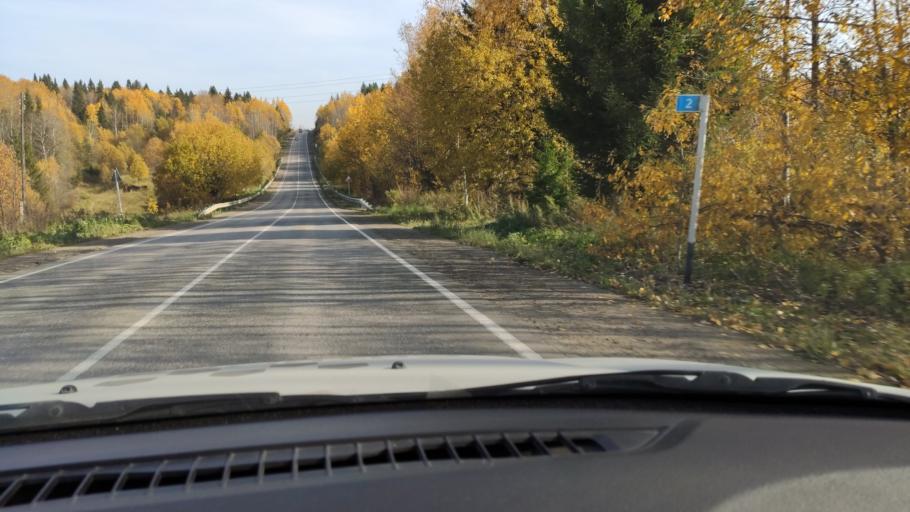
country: RU
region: Perm
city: Novyye Lyady
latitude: 58.0270
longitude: 56.6782
